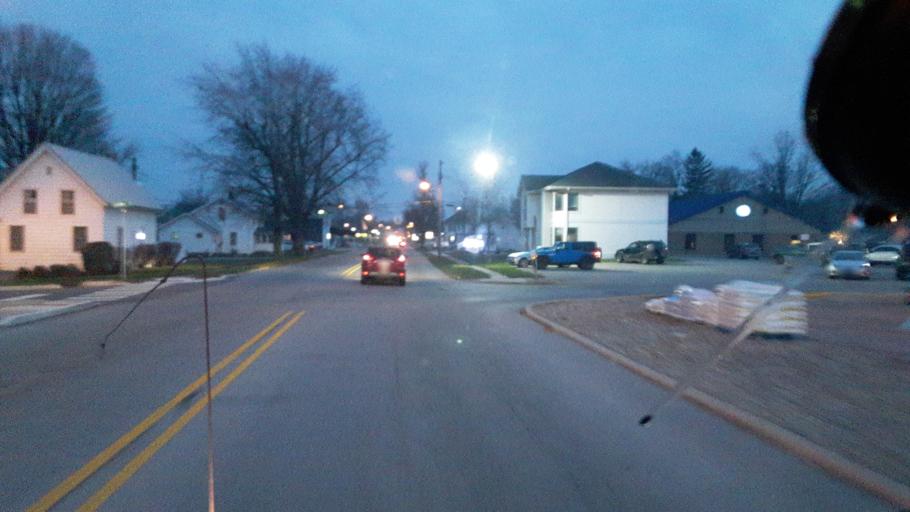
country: US
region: Indiana
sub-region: LaGrange County
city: Lagrange
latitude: 41.6402
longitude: -85.4179
